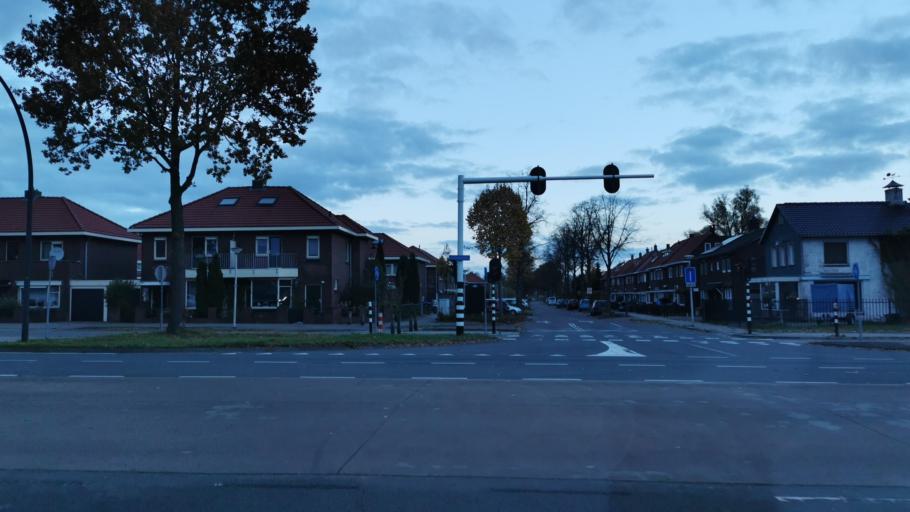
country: NL
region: Overijssel
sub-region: Gemeente Enschede
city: Enschede
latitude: 52.2170
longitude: 6.9454
